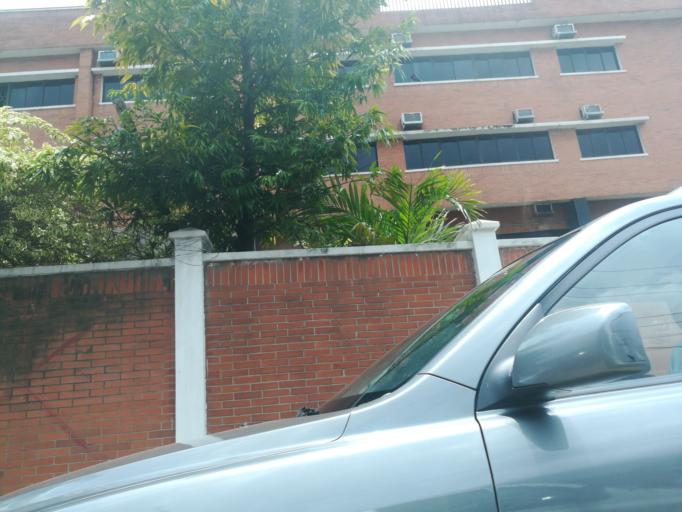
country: NG
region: Lagos
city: Somolu
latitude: 6.5520
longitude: 3.3642
